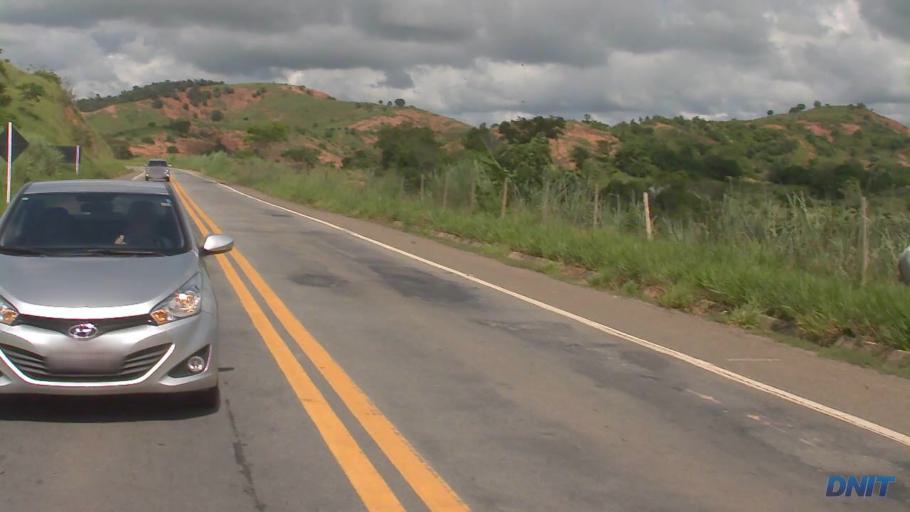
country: BR
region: Minas Gerais
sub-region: Belo Oriente
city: Belo Oriente
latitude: -19.1160
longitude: -42.2097
